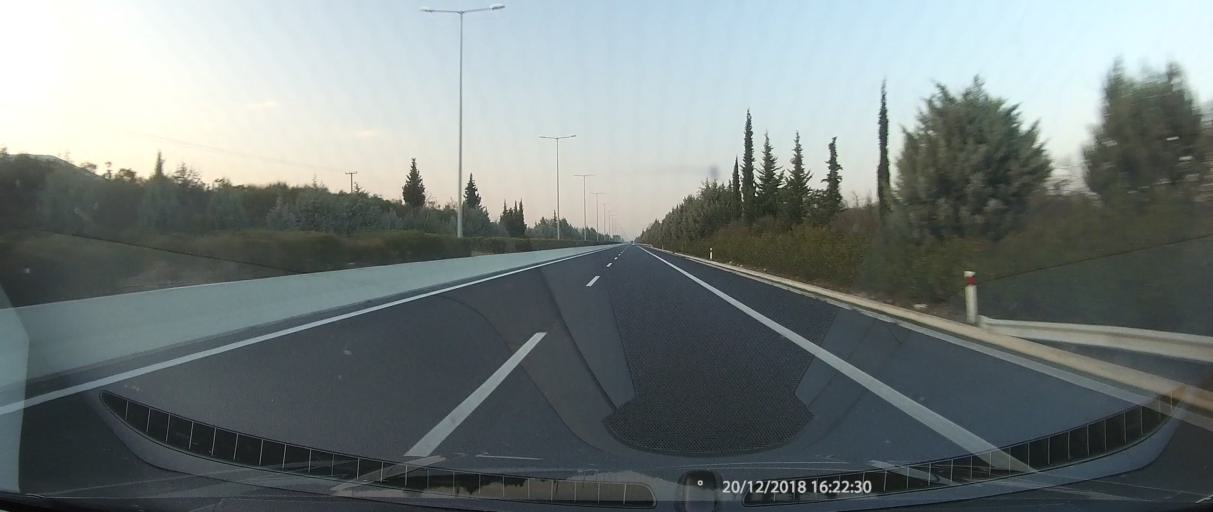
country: GR
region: Thessaly
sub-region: Nomos Magnisias
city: Sourpi
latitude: 39.0714
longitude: 22.8860
